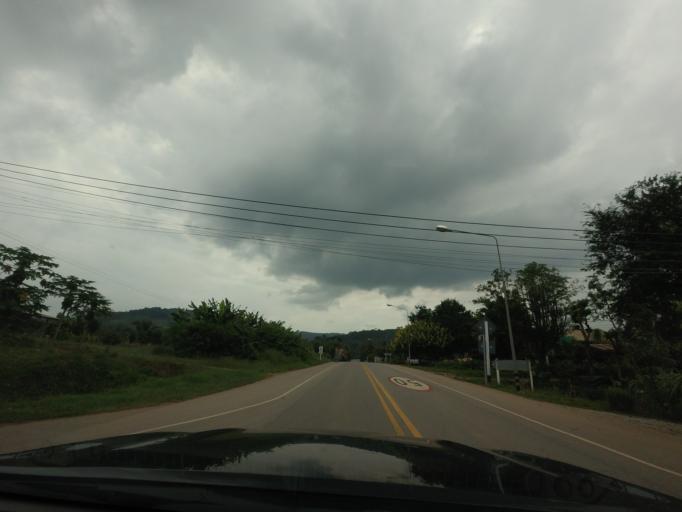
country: TH
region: Loei
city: Dan Sai
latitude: 17.2894
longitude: 101.2439
